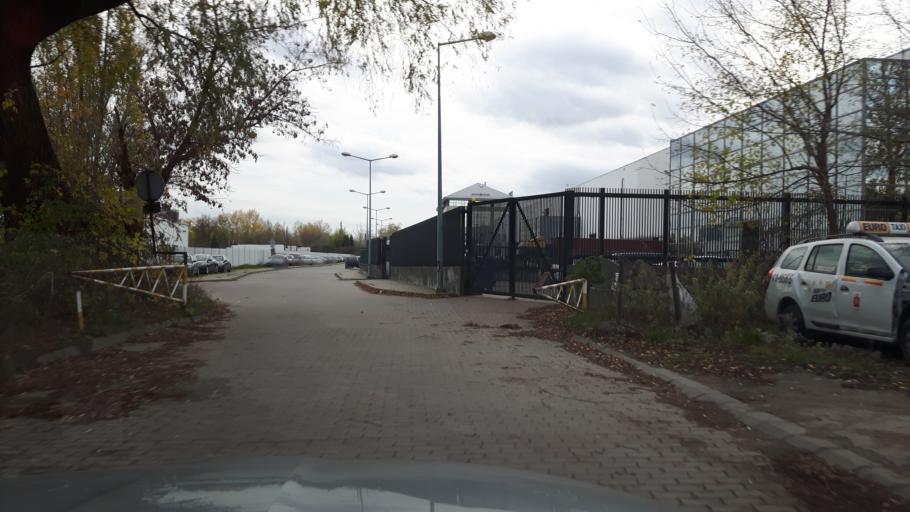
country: PL
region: Masovian Voivodeship
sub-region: Warszawa
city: Wlochy
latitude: 52.1741
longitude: 20.9901
